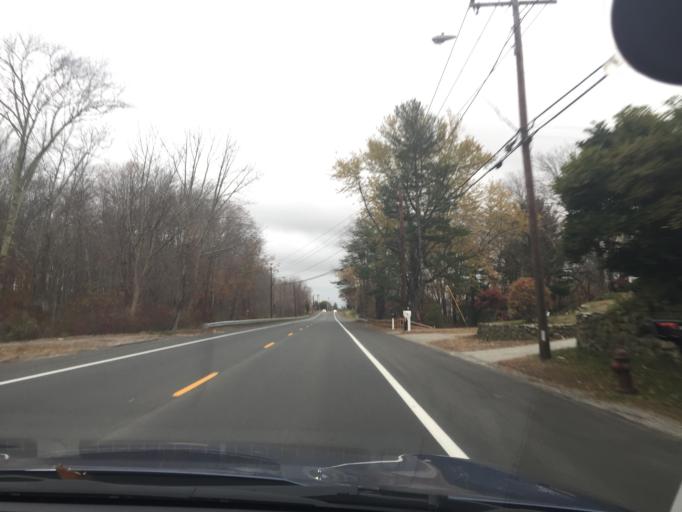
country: US
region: Rhode Island
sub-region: Providence County
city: North Scituate
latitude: 41.7905
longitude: -71.5577
